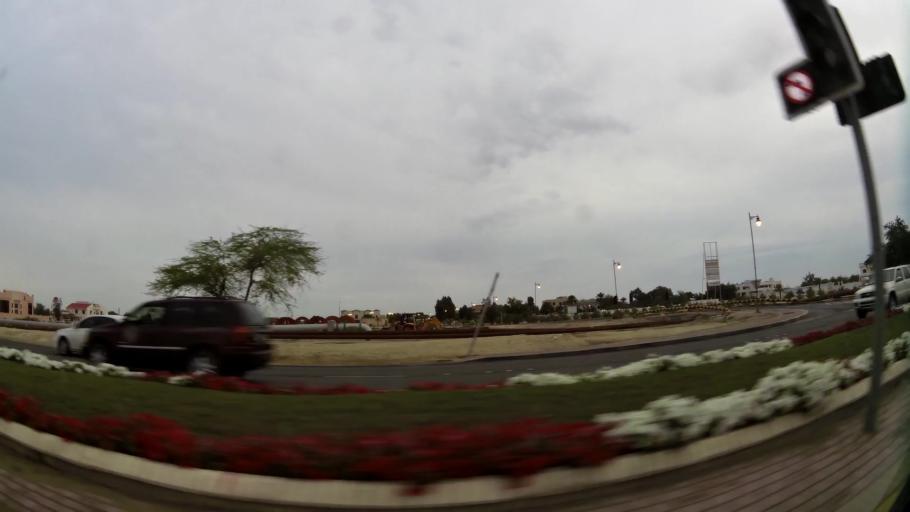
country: BH
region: Northern
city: Ar Rifa'
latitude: 26.1351
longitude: 50.5322
